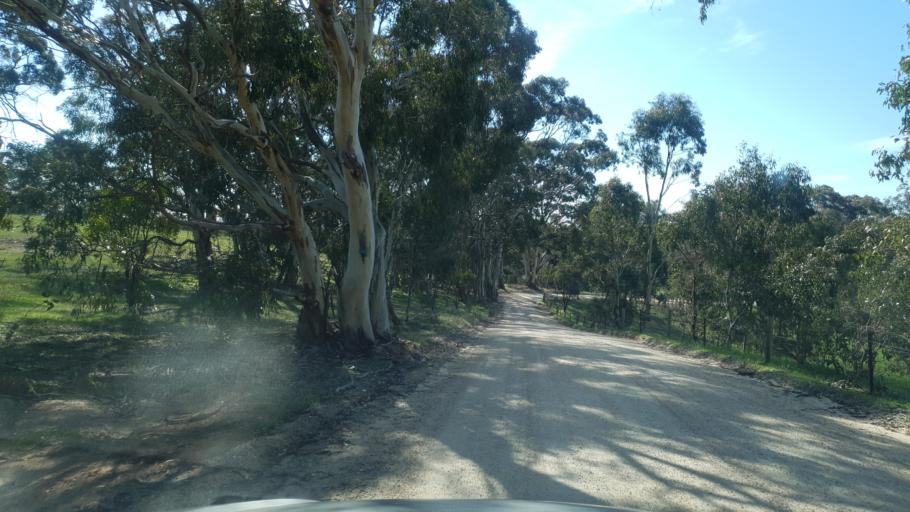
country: AU
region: South Australia
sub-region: Playford
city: One Tree Hill
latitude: -34.6542
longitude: 138.8157
